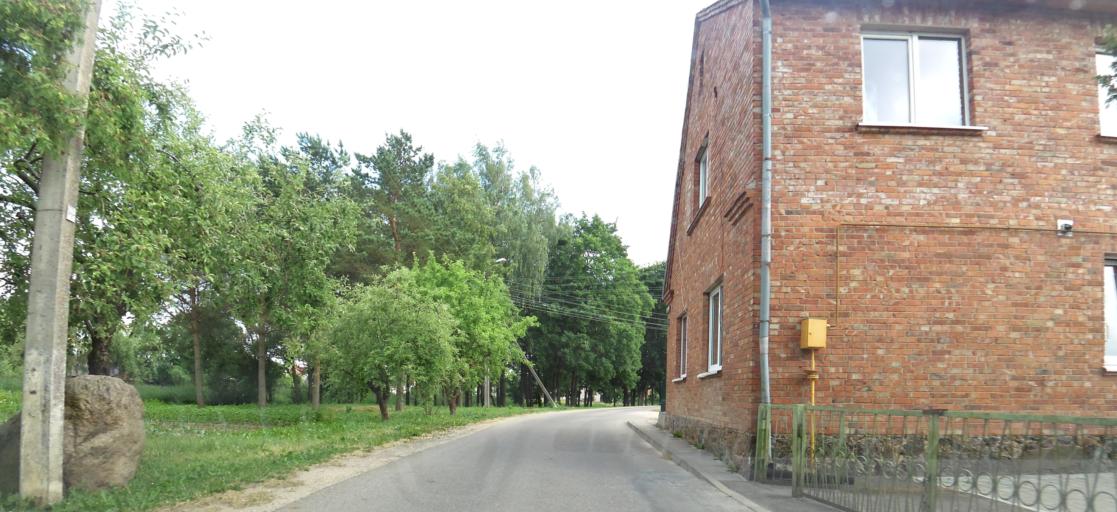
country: LT
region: Panevezys
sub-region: Birzai
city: Birzai
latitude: 56.2046
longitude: 24.7649
